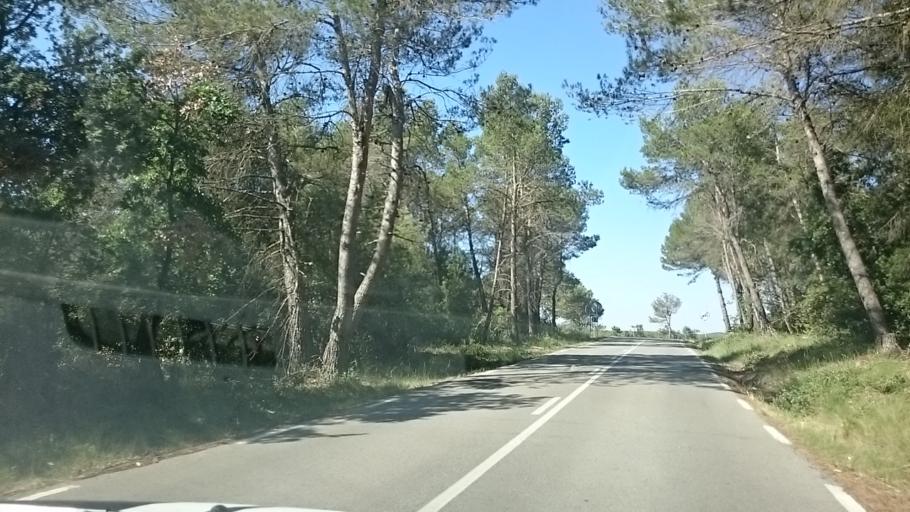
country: ES
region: Catalonia
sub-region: Provincia de Tarragona
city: Querol
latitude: 41.4182
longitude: 1.4939
